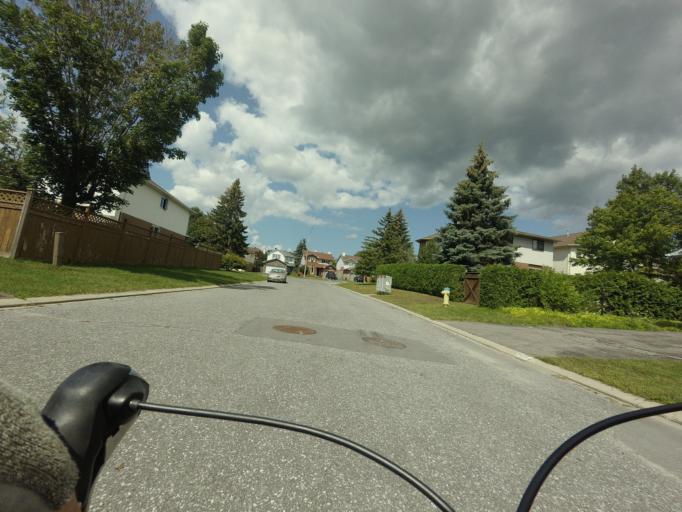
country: CA
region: Ontario
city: Bells Corners
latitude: 45.2884
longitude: -75.8606
